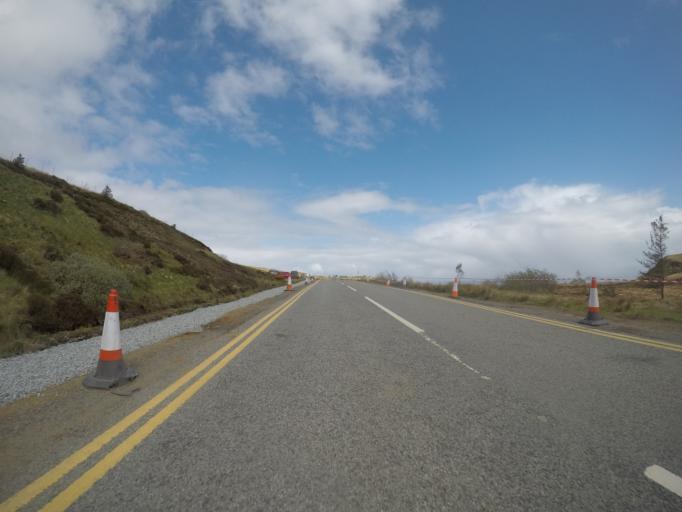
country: GB
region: Scotland
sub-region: Highland
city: Portree
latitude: 57.4970
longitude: -6.1592
